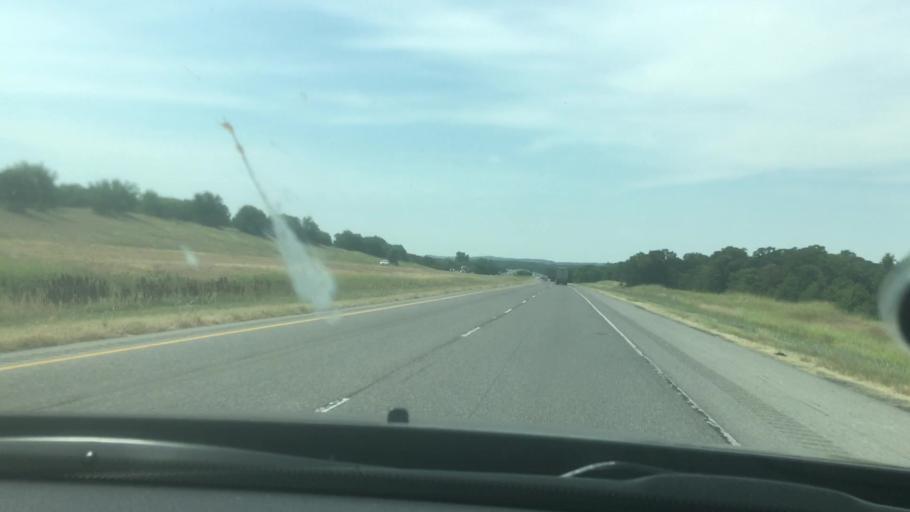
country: US
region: Oklahoma
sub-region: Murray County
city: Davis
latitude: 34.5428
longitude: -97.1900
